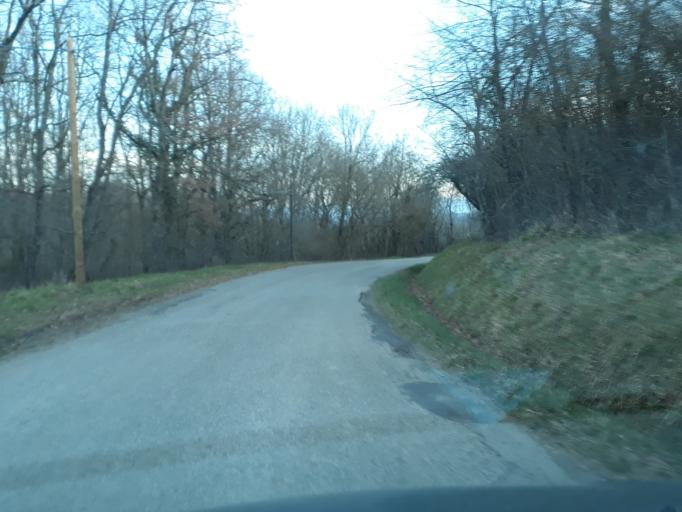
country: FR
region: Midi-Pyrenees
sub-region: Departement de la Haute-Garonne
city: Montesquieu-Volvestre
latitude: 43.1747
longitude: 1.3217
